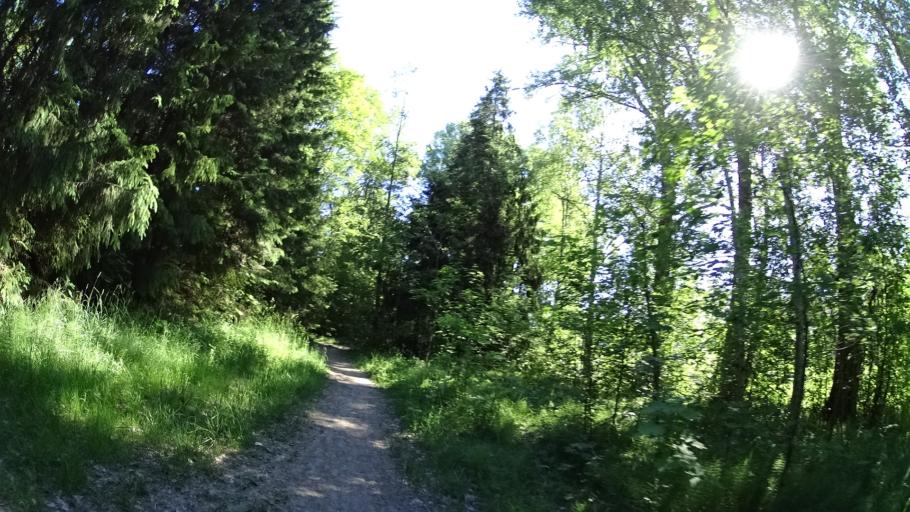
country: FI
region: Uusimaa
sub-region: Helsinki
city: Kauniainen
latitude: 60.2097
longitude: 24.7171
